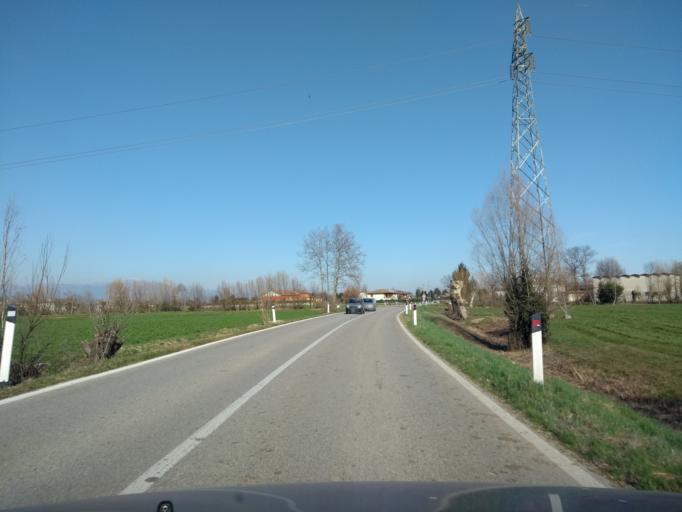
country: IT
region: Veneto
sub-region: Provincia di Padova
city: San Pietro in Gu
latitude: 45.6089
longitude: 11.6477
